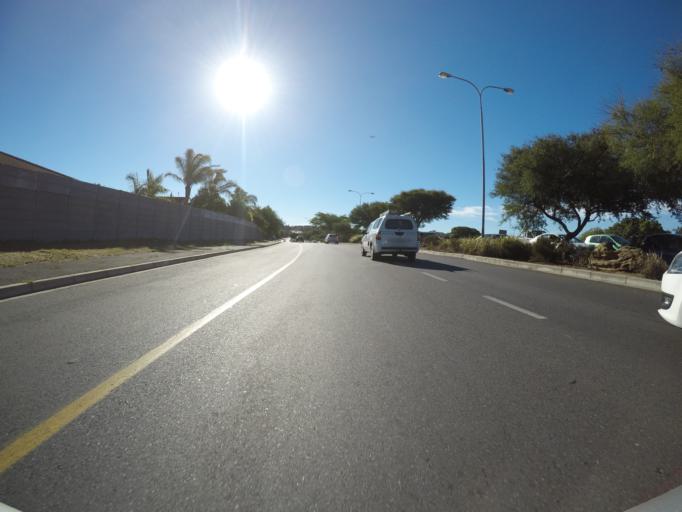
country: ZA
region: Western Cape
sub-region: City of Cape Town
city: Kraaifontein
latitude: -33.8743
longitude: 18.6558
